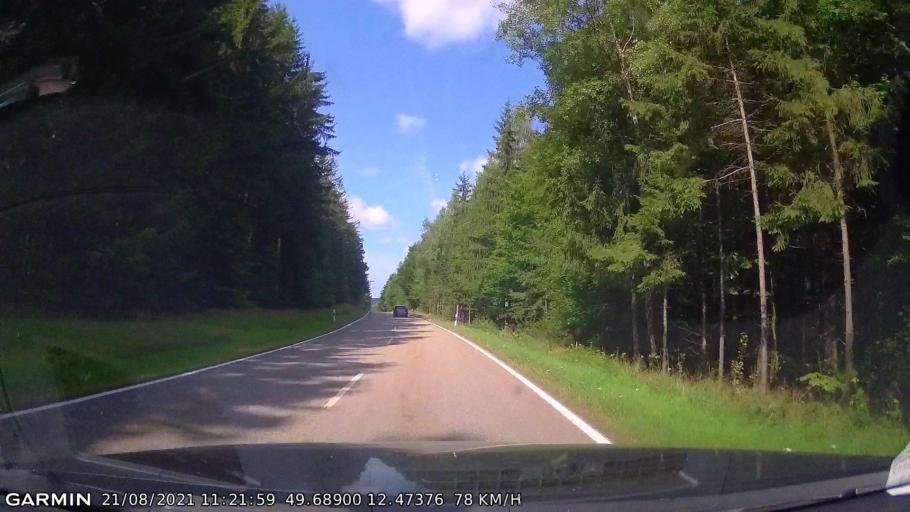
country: DE
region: Bavaria
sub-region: Upper Palatinate
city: Waidhaus
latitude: 49.6890
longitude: 12.4738
